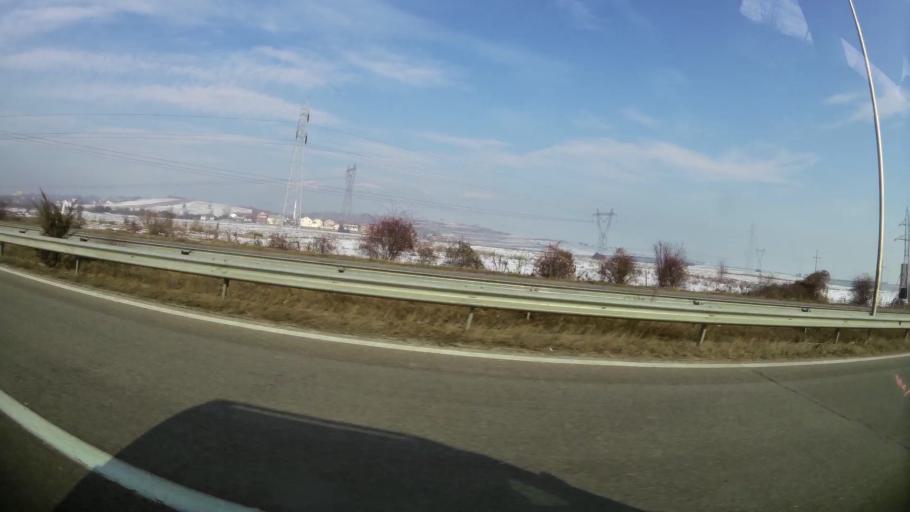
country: MK
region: Butel
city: Butel
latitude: 42.0385
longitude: 21.4646
